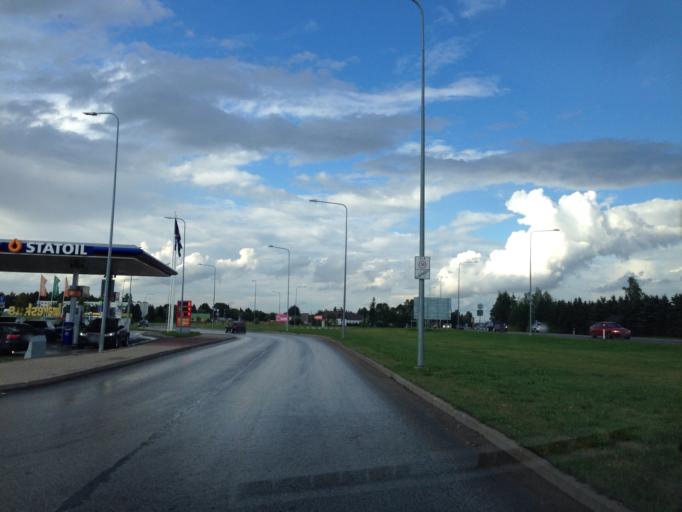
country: EE
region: Tartu
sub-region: Tartu linn
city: Tartu
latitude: 58.3601
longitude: 26.6780
